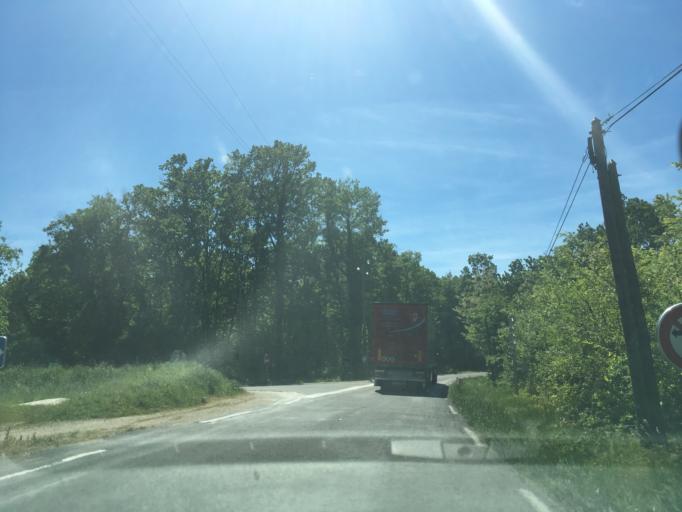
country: FR
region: Aquitaine
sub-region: Departement de la Gironde
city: Lesparre-Medoc
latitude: 45.2656
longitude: -0.8968
